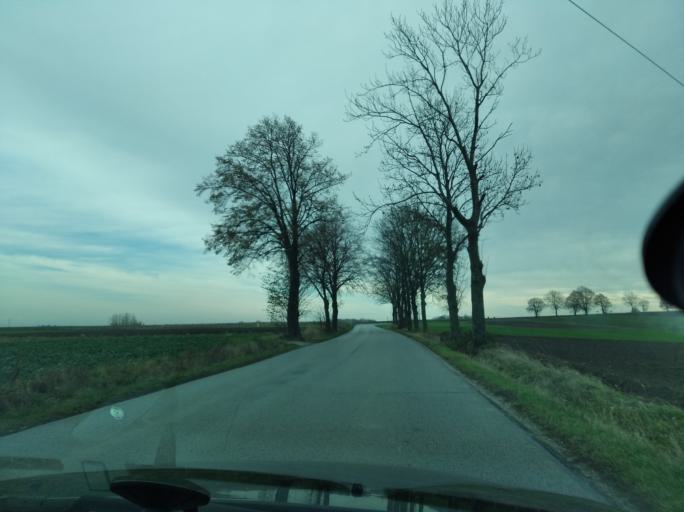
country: PL
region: Subcarpathian Voivodeship
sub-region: Powiat lancucki
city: Wysoka
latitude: 50.0244
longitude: 22.2565
